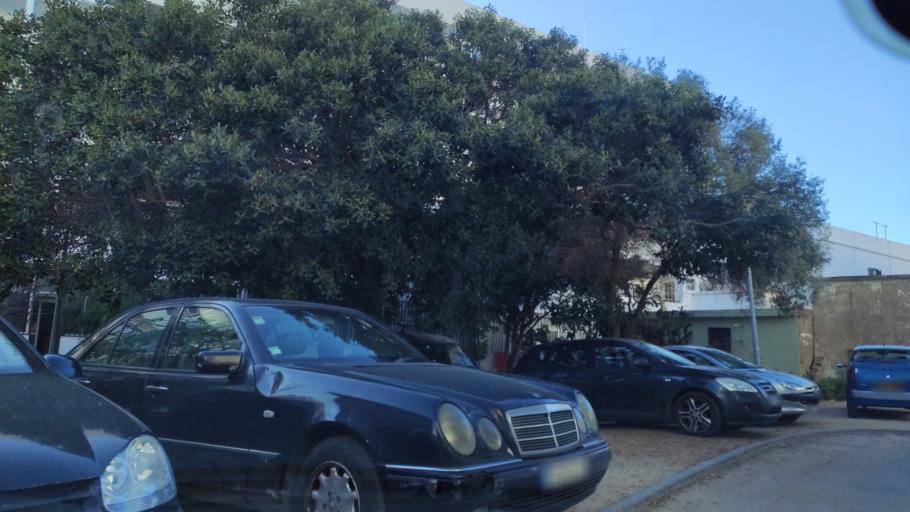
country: PT
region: Faro
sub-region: Faro
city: Faro
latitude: 37.0149
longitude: -7.9219
